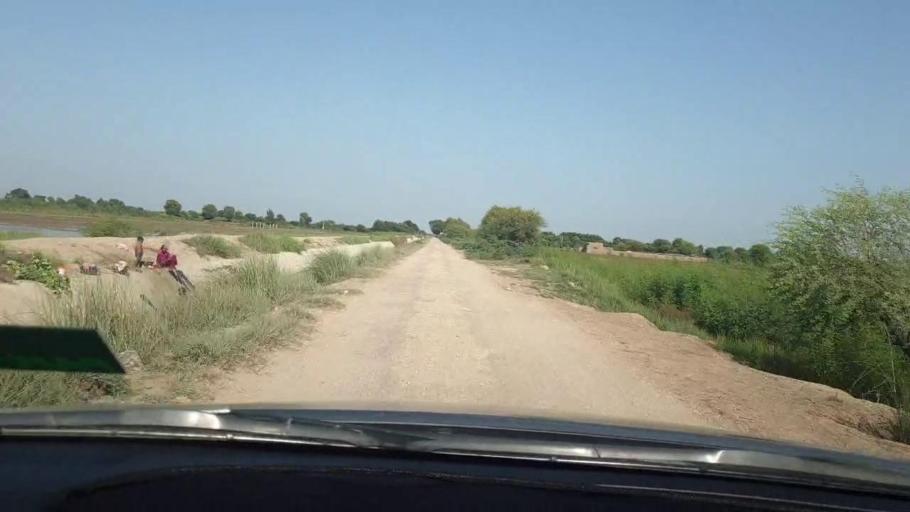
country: PK
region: Sindh
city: Naukot
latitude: 24.9311
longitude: 69.2715
